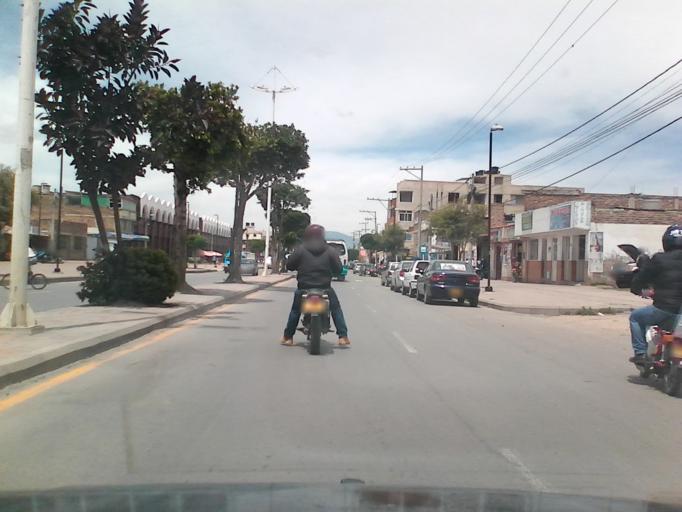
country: CO
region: Boyaca
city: Sogamoso
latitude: 5.7204
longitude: -72.9378
